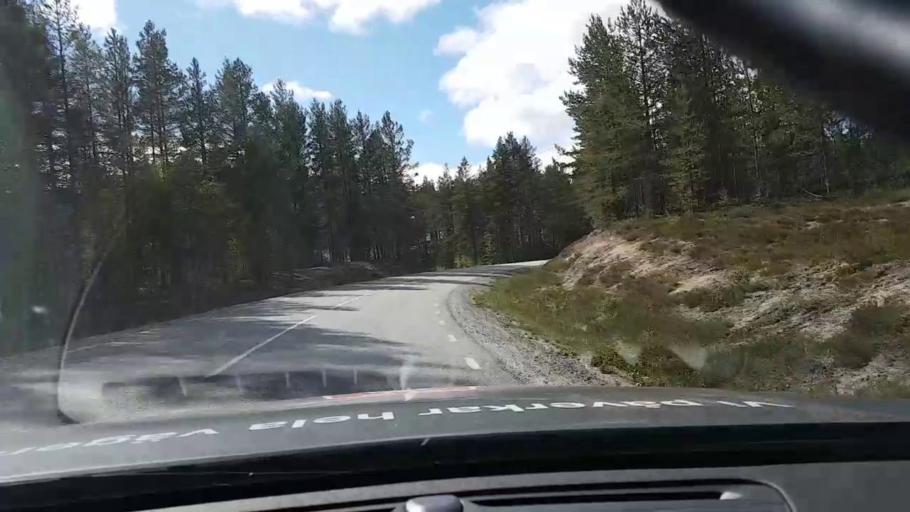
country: SE
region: Vaesternorrland
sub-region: OErnskoeldsviks Kommun
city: Bredbyn
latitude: 63.6739
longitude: 17.8059
